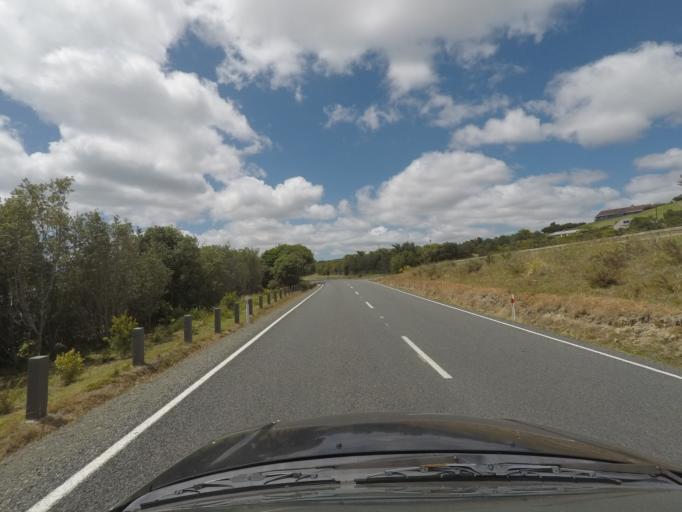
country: NZ
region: Northland
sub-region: Whangarei
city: Ruakaka
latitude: -36.0173
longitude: 174.4906
